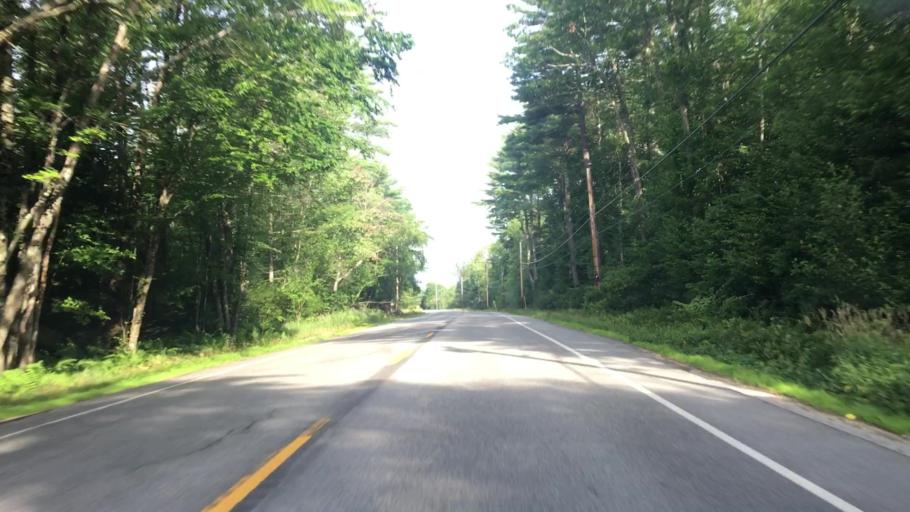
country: US
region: Maine
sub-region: York County
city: Limington
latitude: 43.7671
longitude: -70.7166
